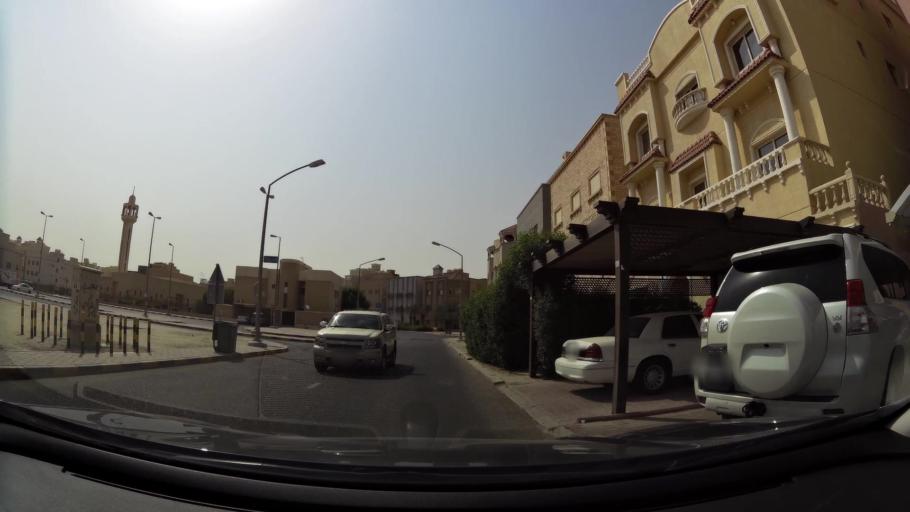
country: KW
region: Muhafazat al Jahra'
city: Al Jahra'
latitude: 29.3239
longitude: 47.7367
